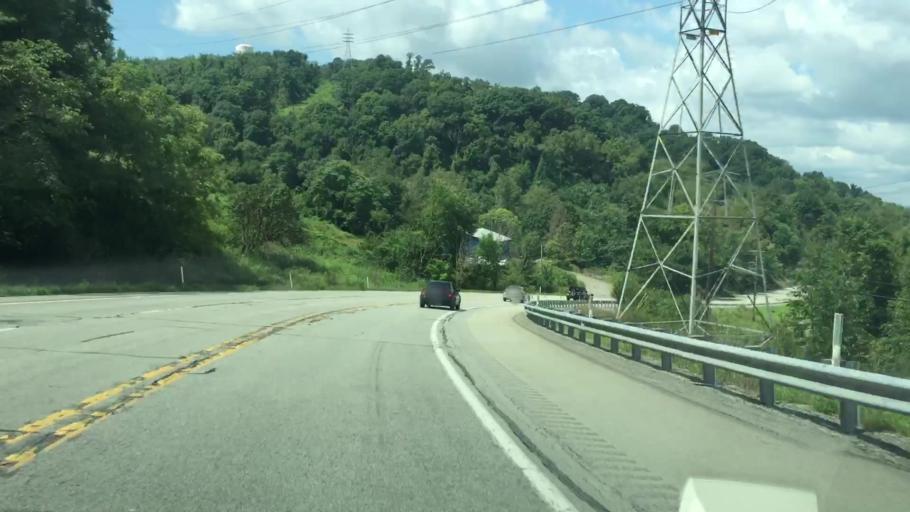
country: US
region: Pennsylvania
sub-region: Allegheny County
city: Oakmont
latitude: 40.5528
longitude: -79.8479
